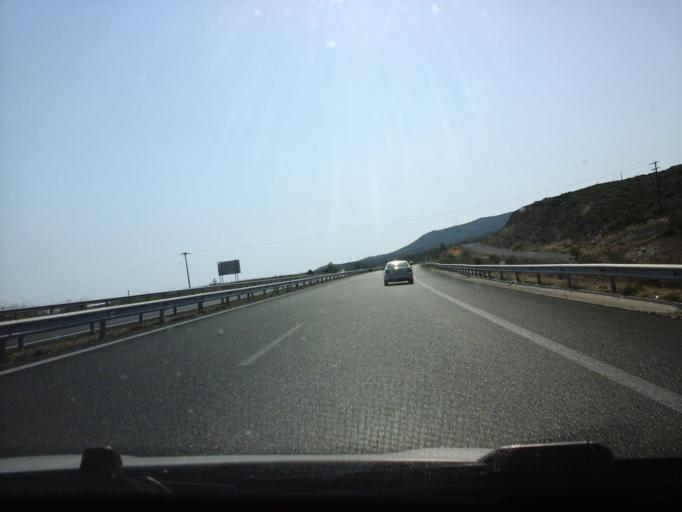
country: GR
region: East Macedonia and Thrace
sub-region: Nomos Evrou
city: Alexandroupoli
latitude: 40.8677
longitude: 25.7768
